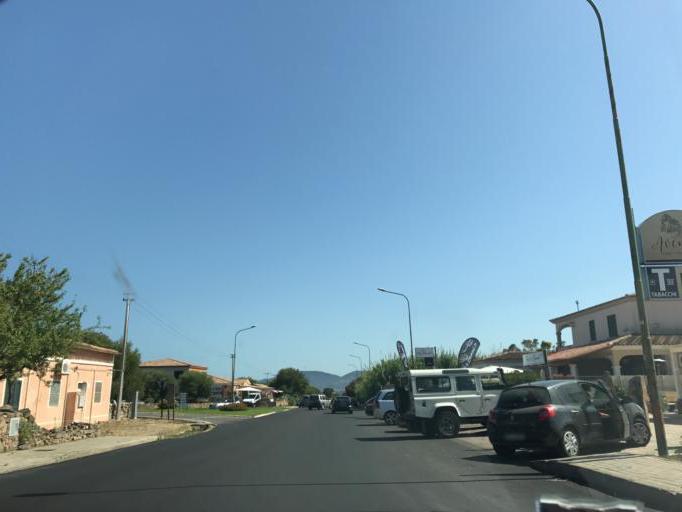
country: IT
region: Sardinia
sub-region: Provincia di Olbia-Tempio
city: San Teodoro
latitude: 40.8200
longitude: 9.6593
